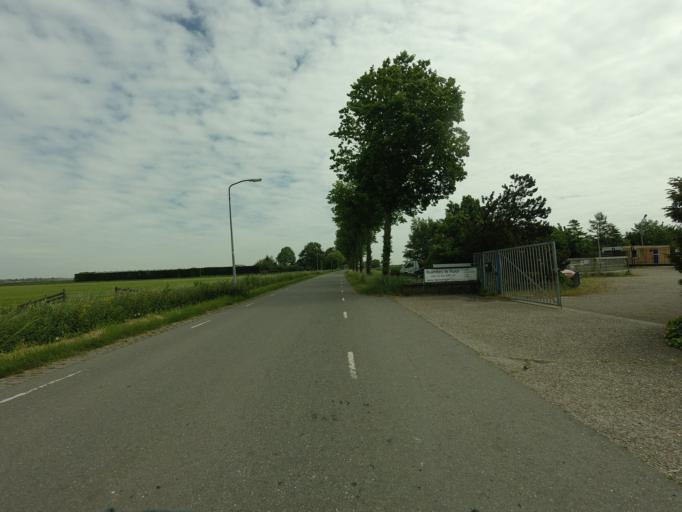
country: NL
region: North Holland
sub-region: Gemeente Hoorn
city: Hoorn
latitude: 52.6945
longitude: 5.0766
